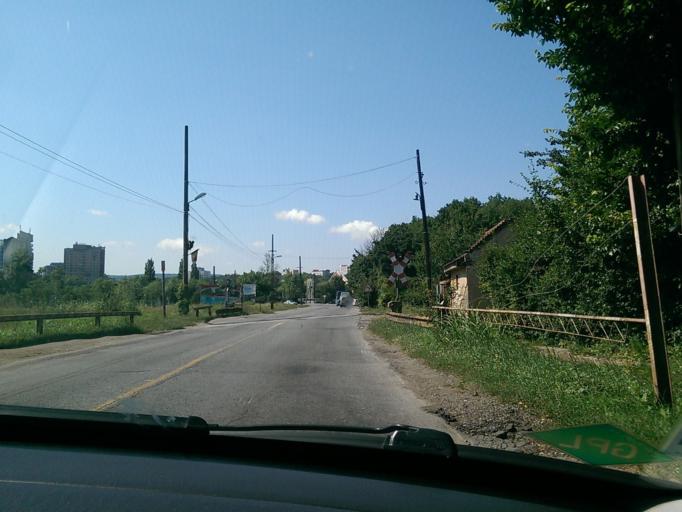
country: RO
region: Bihor
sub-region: Comuna Sanmartin
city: Sanmartin
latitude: 46.9983
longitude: 21.9792
